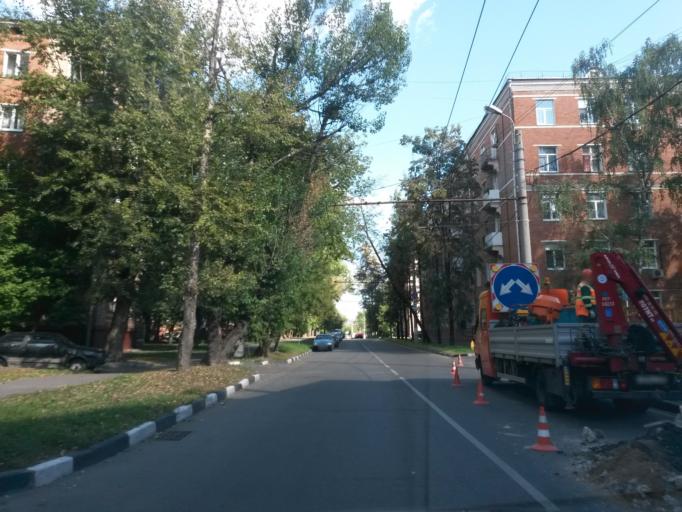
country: RU
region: Moscow
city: Kotlovka
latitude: 55.6671
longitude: 37.6175
